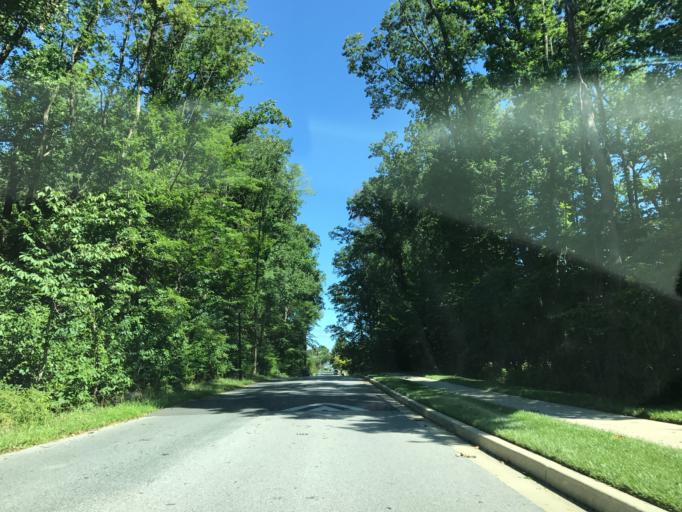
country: US
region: Maryland
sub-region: Howard County
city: Ilchester
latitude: 39.2585
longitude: -76.7575
